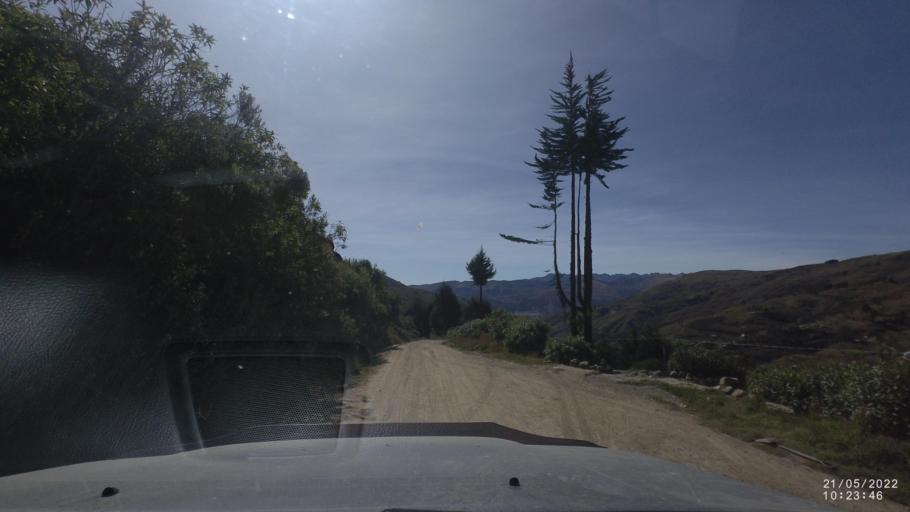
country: BO
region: Cochabamba
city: Colomi
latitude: -17.3244
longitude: -65.9503
